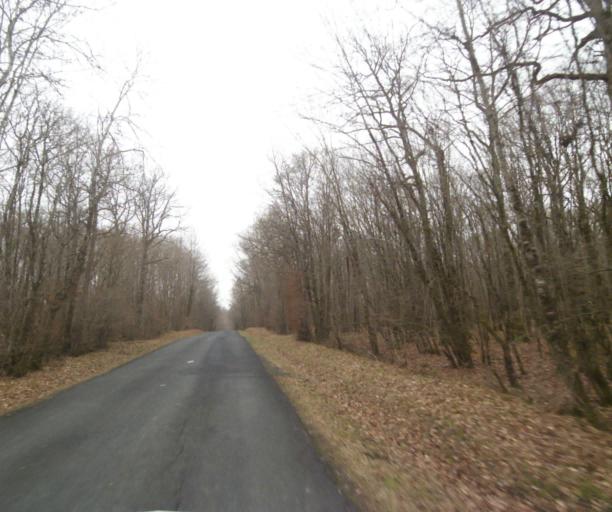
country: FR
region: Champagne-Ardenne
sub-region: Departement de la Haute-Marne
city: Bienville
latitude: 48.5602
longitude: 5.0042
